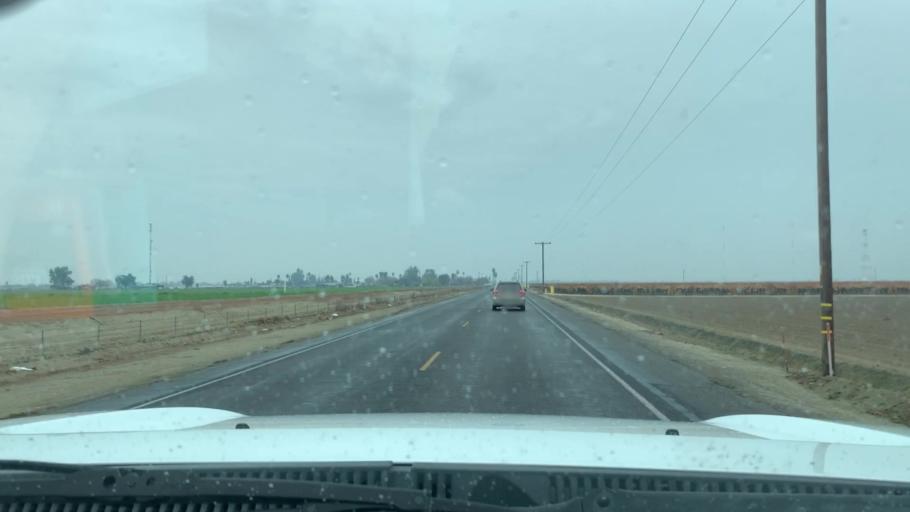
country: US
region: California
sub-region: Kern County
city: Delano
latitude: 35.7613
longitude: -119.3001
